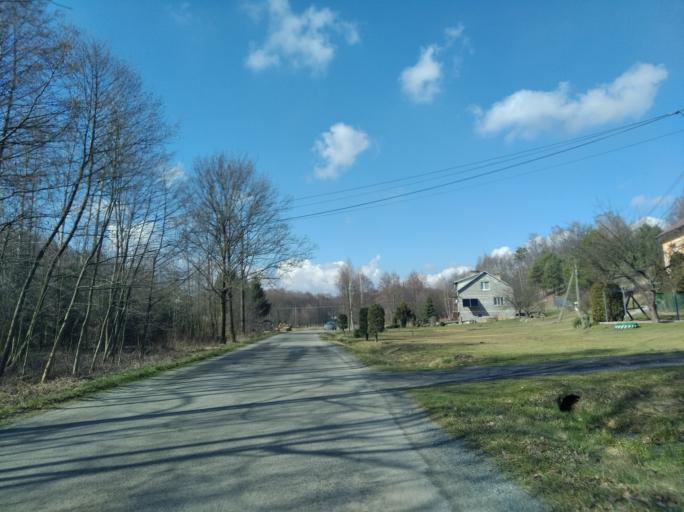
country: PL
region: Subcarpathian Voivodeship
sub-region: Powiat debicki
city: Brzostek
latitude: 49.8929
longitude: 21.4922
